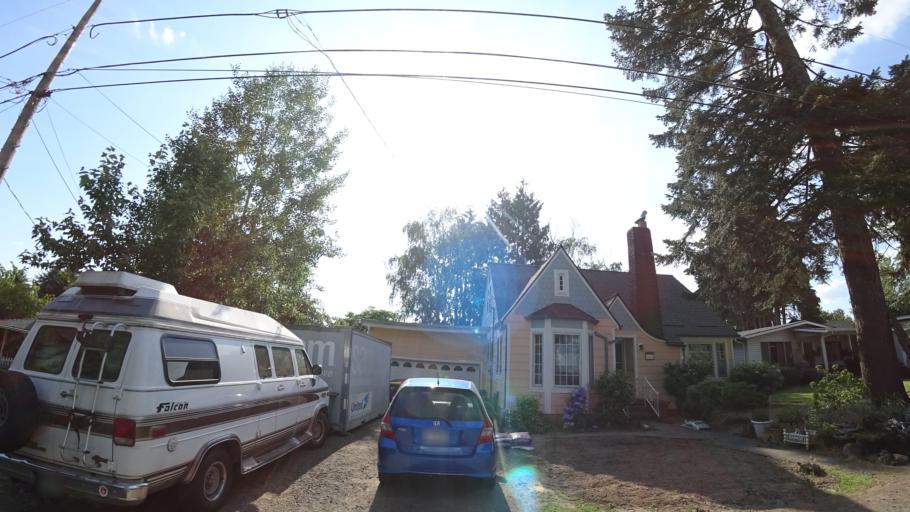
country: US
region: Oregon
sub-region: Washington County
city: Garden Home-Whitford
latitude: 45.4650
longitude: -122.7443
